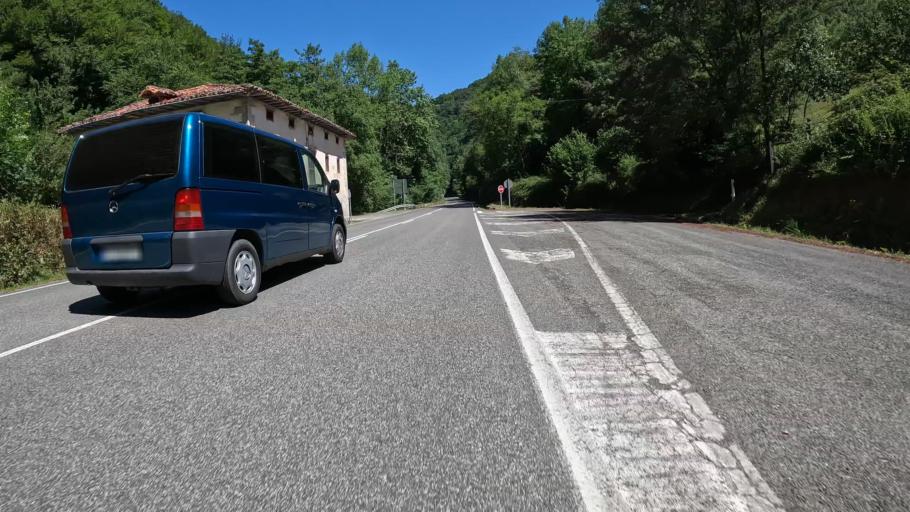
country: ES
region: Basque Country
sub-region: Provincia de Guipuzcoa
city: Oreja
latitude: 43.0707
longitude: -2.0115
